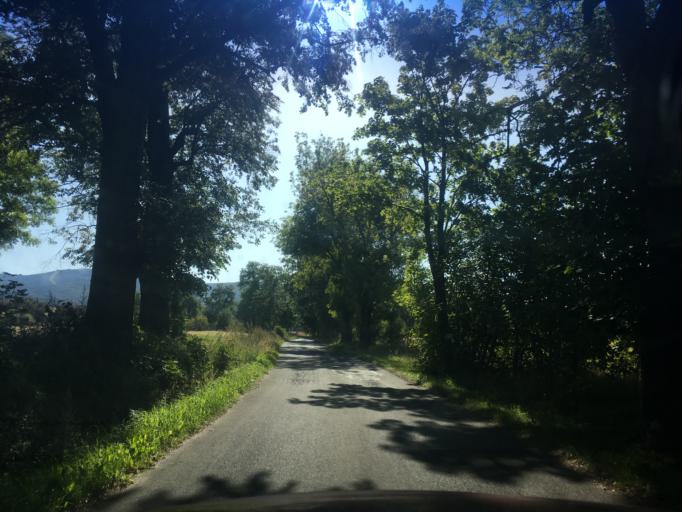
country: PL
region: Lower Silesian Voivodeship
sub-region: Powiat lubanski
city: Swieradow-Zdroj
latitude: 50.9484
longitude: 15.3144
